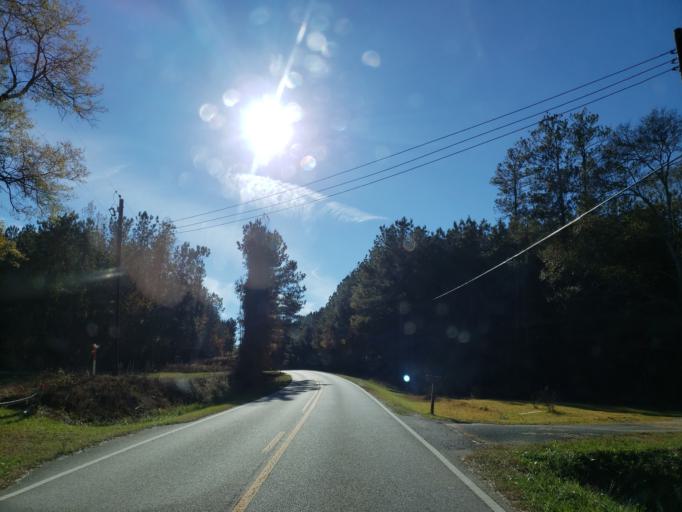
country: US
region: Alabama
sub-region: Cleburne County
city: Heflin
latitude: 33.5720
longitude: -85.6433
